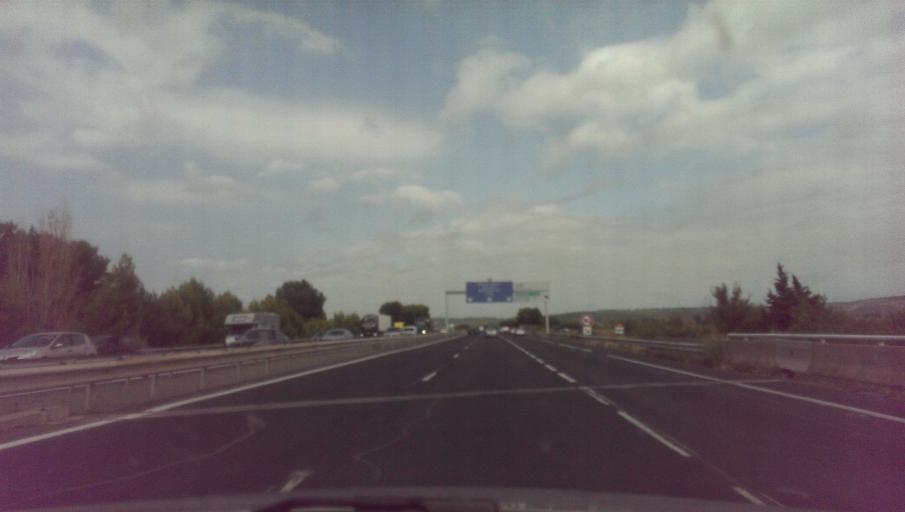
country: FR
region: Languedoc-Roussillon
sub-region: Departement de l'Aude
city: Narbonne
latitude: 43.1741
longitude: 3.0280
